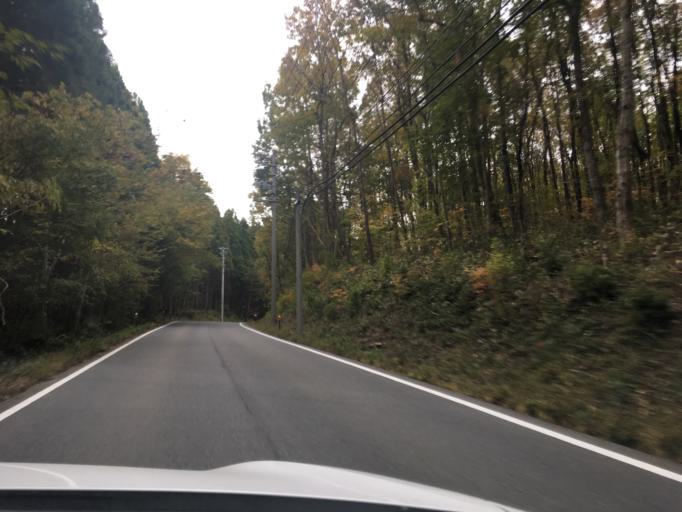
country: JP
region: Fukushima
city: Iwaki
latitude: 37.1112
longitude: 140.7804
